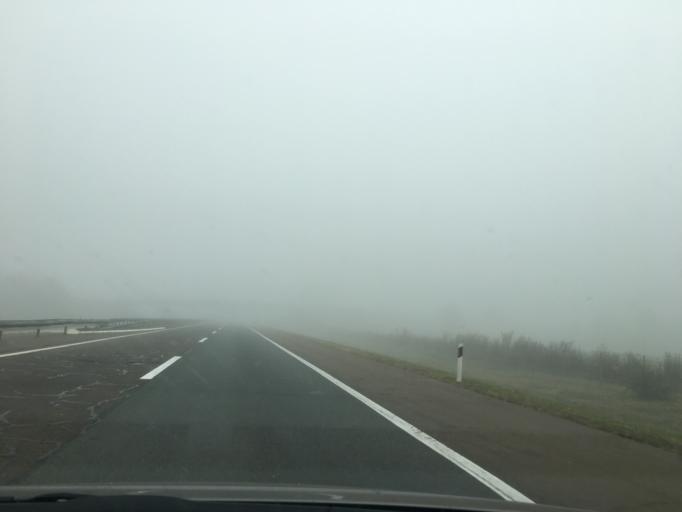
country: RS
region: Autonomna Pokrajina Vojvodina
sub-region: Sremski Okrug
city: Stara Pazova
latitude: 45.0261
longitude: 20.1904
